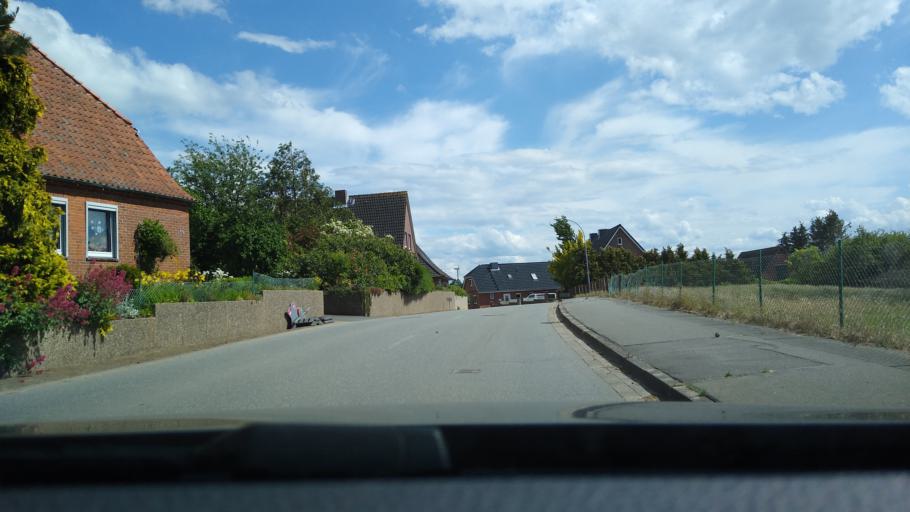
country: DE
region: Schleswig-Holstein
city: Kabelhorst
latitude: 54.2288
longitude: 10.9295
